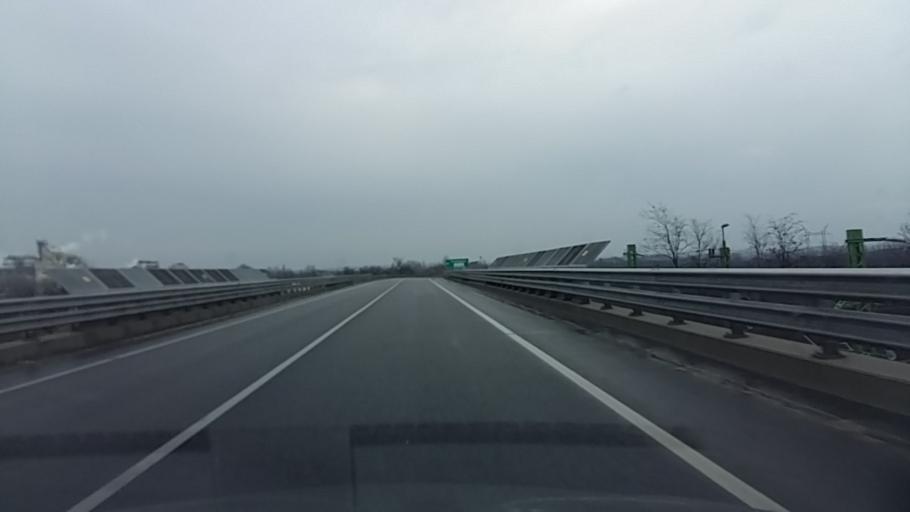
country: HU
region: Fejer
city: Sarosd
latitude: 47.0848
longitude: 18.7065
